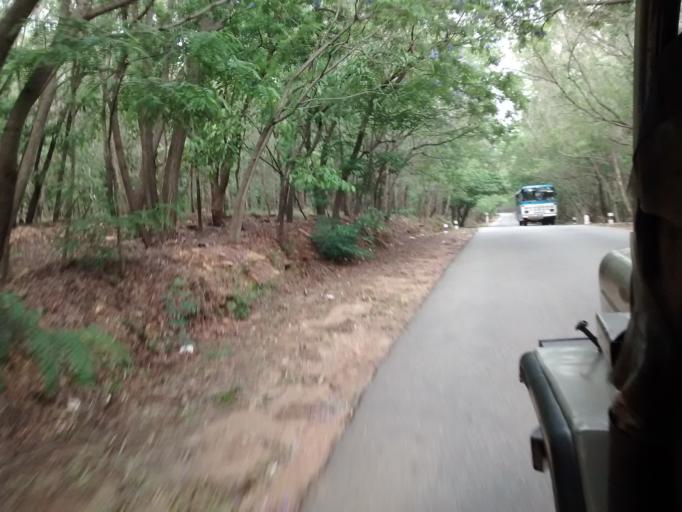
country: IN
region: Andhra Pradesh
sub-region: Chittoor
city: Tirumala
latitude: 13.7013
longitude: 79.3479
